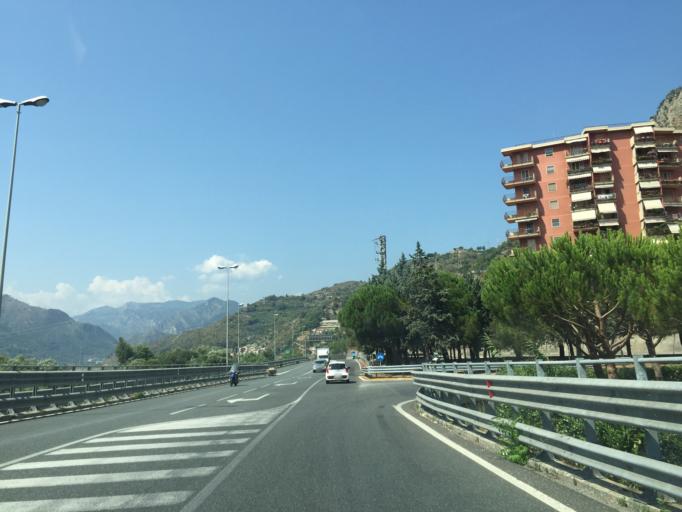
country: IT
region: Liguria
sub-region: Provincia di Imperia
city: Ventimiglia
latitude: 43.8091
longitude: 7.5923
